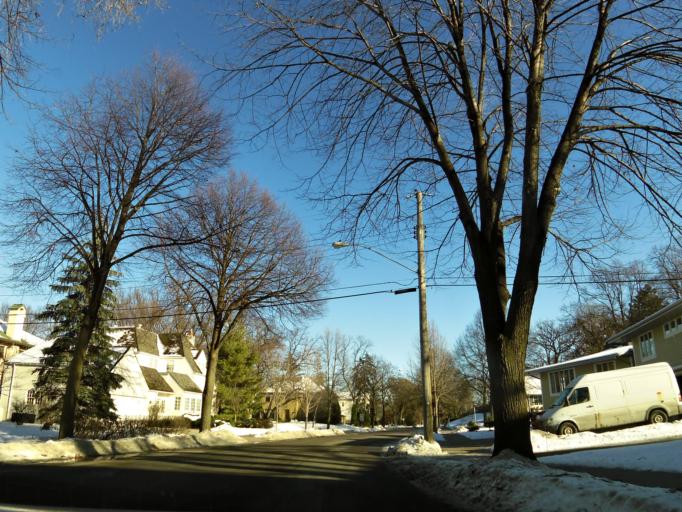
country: US
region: Minnesota
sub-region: Hennepin County
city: Saint Louis Park
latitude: 44.9341
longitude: -93.3236
